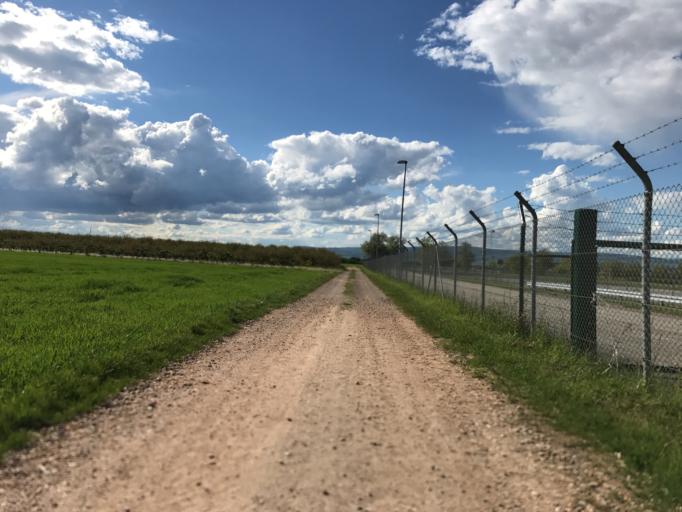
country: DE
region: Rheinland-Pfalz
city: Wackernheim
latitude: 49.9639
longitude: 8.1180
